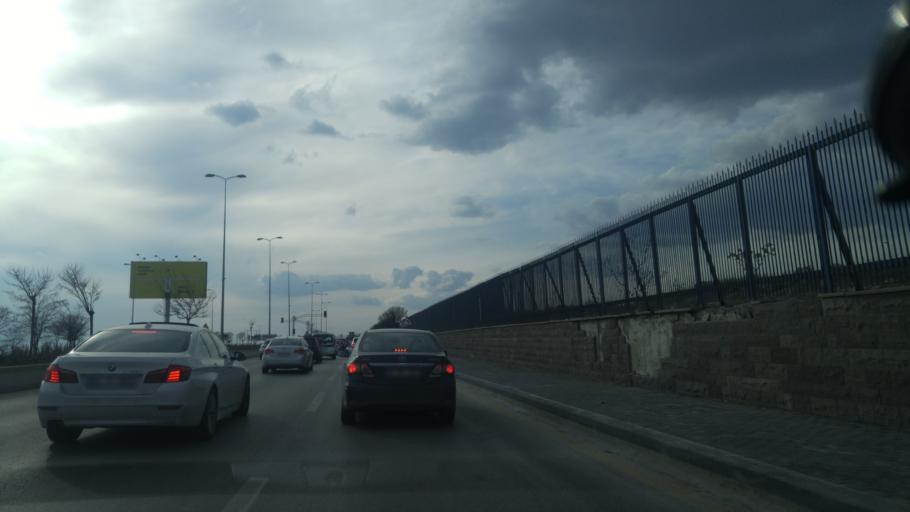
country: TR
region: Ankara
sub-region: Goelbasi
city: Golbasi
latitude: 39.8359
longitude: 32.7666
